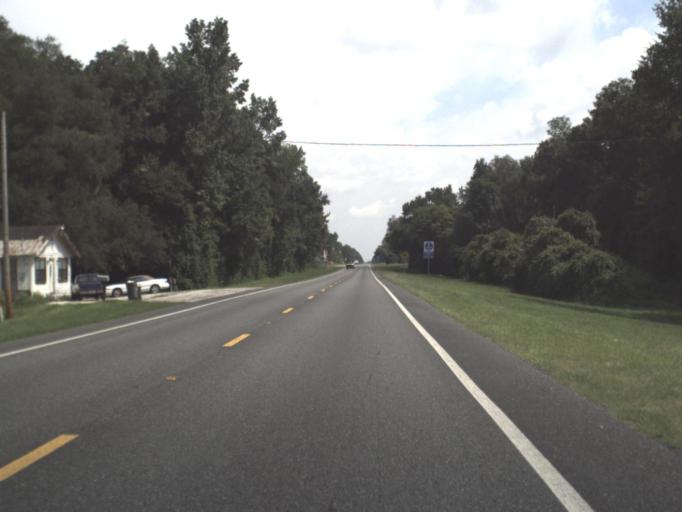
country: US
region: Florida
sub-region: Alachua County
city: High Springs
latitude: 29.8582
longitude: -82.6085
